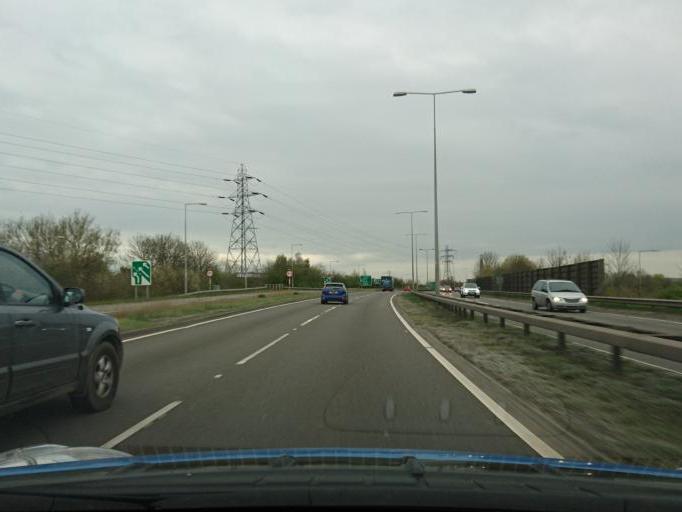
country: GB
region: England
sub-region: Stoke-on-Trent
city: Stoke-on-Trent
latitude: 53.0002
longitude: -2.1792
